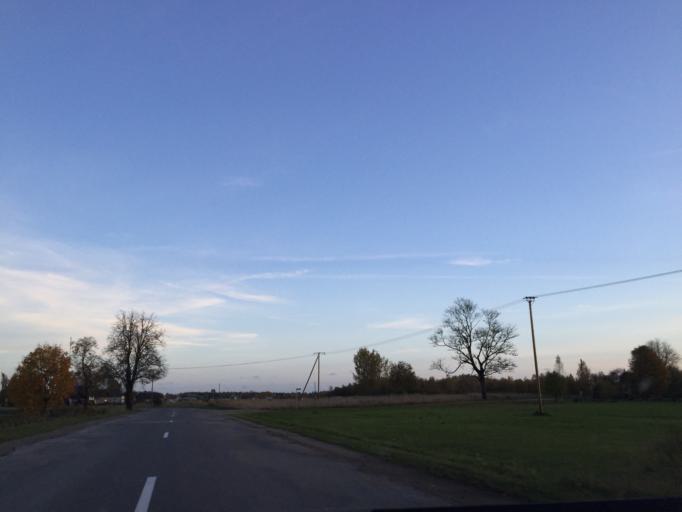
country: LV
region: Malpils
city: Malpils
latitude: 56.8955
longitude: 24.9288
